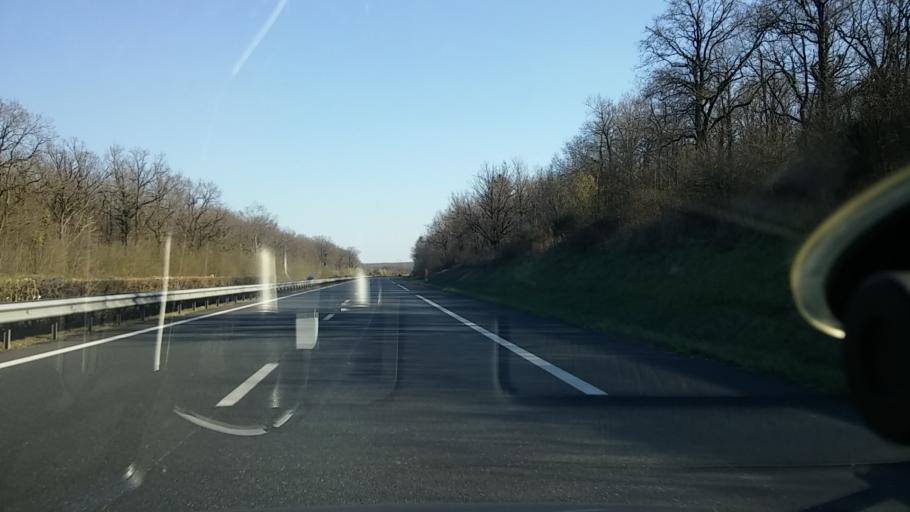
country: FR
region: Centre
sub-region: Departement de l'Indre
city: Saint-Maur
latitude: 46.7877
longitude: 1.6251
